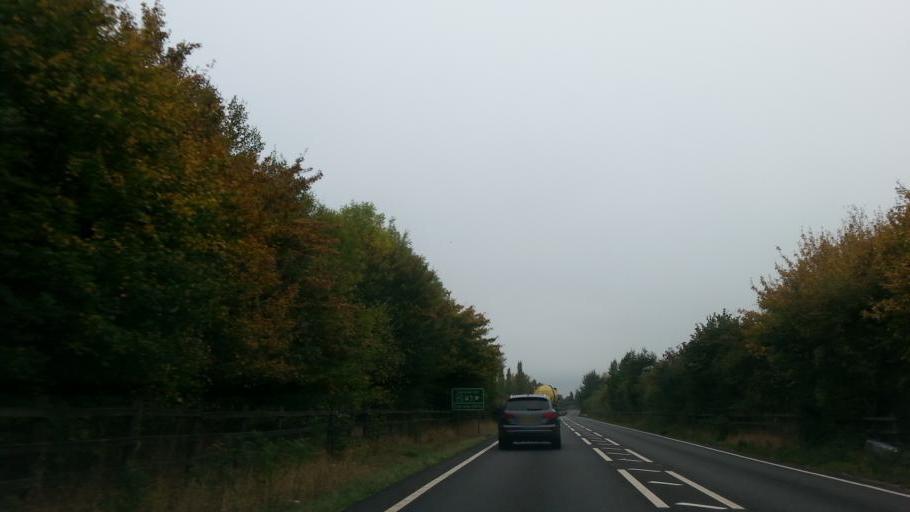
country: GB
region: England
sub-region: Northamptonshire
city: Oundle
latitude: 52.5113
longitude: -0.4185
